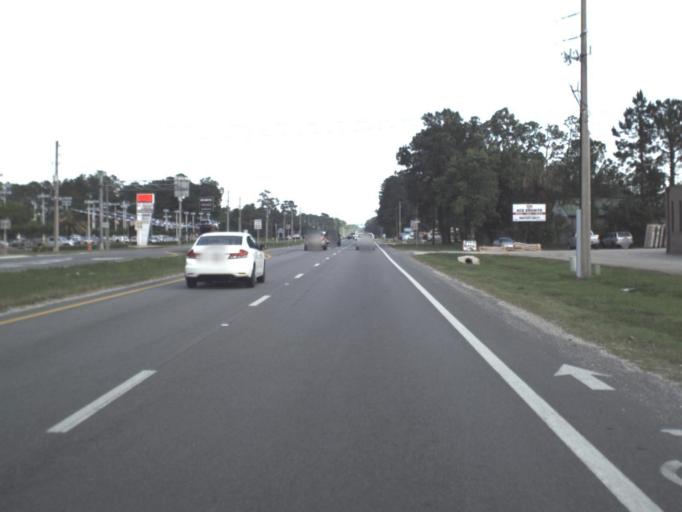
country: US
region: Florida
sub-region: Saint Johns County
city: Fruit Cove
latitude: 30.1622
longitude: -81.5358
